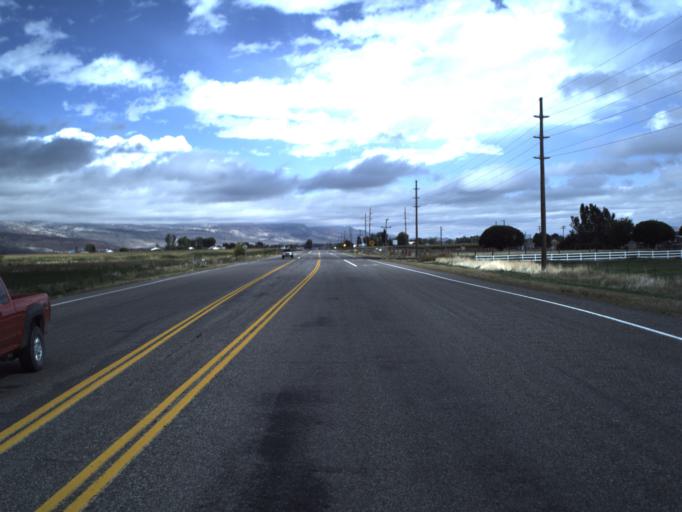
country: US
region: Utah
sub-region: Sevier County
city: Monroe
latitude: 38.7002
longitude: -112.1116
